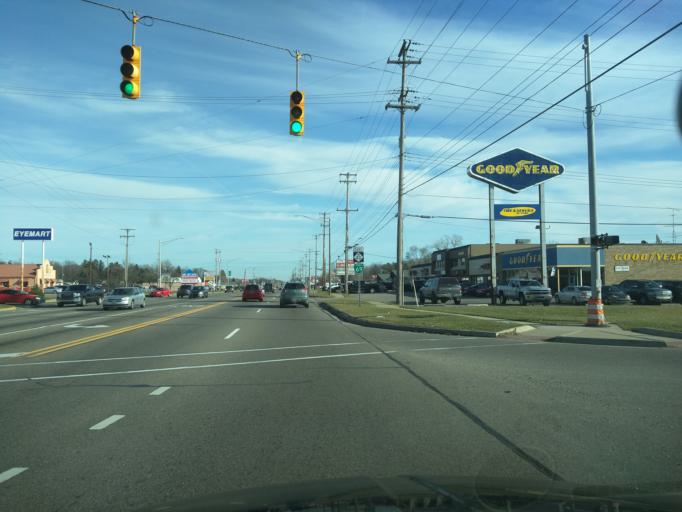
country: US
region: Michigan
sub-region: Eaton County
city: Waverly
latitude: 42.7409
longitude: -84.6221
